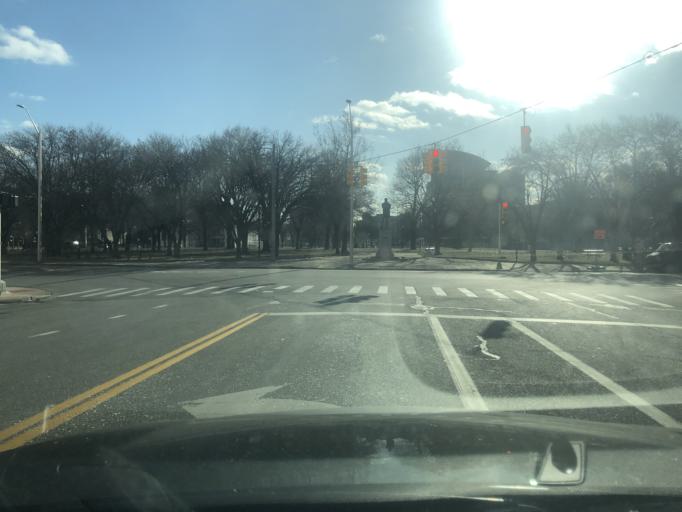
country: US
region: Michigan
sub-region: Wayne County
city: Detroit
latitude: 42.3415
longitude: -83.0614
